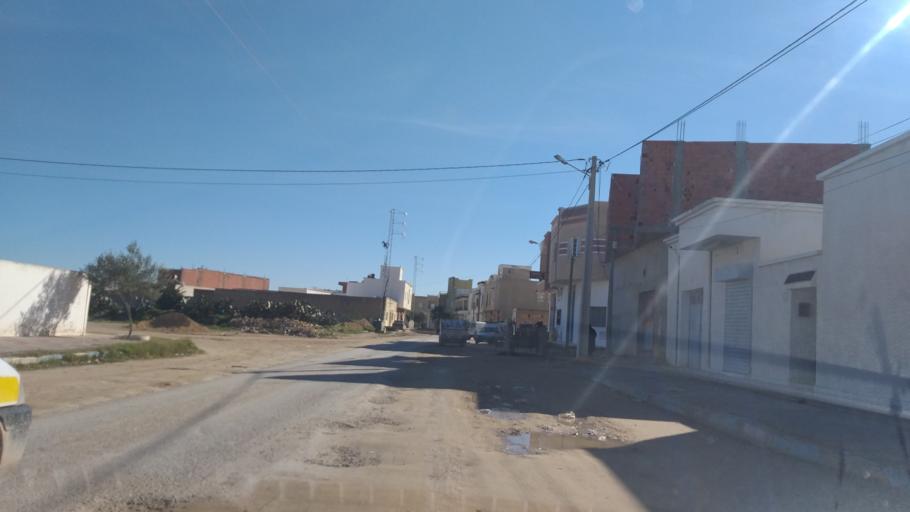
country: TN
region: Al Mahdiyah
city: El Jem
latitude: 35.2936
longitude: 10.7152
